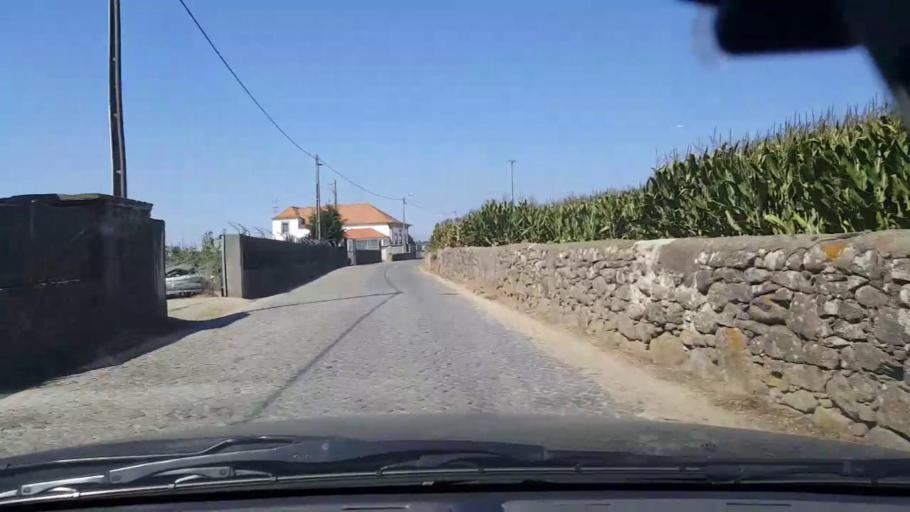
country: PT
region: Porto
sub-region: Matosinhos
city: Lavra
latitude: 41.2777
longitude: -8.7118
